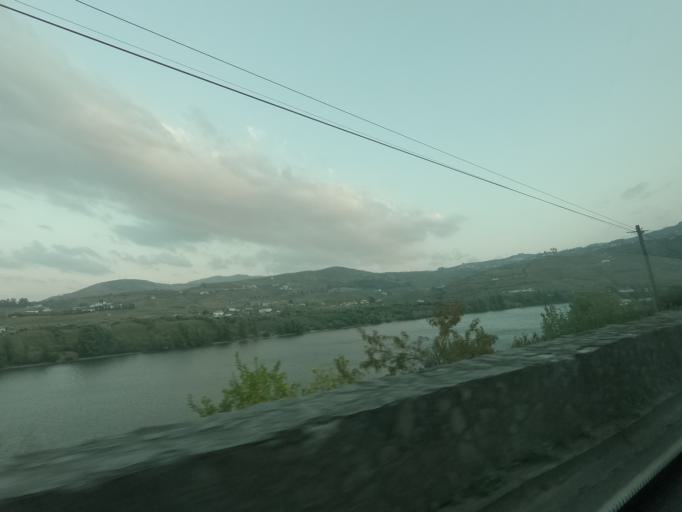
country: PT
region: Vila Real
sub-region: Peso da Regua
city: Godim
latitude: 41.1555
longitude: -7.8085
